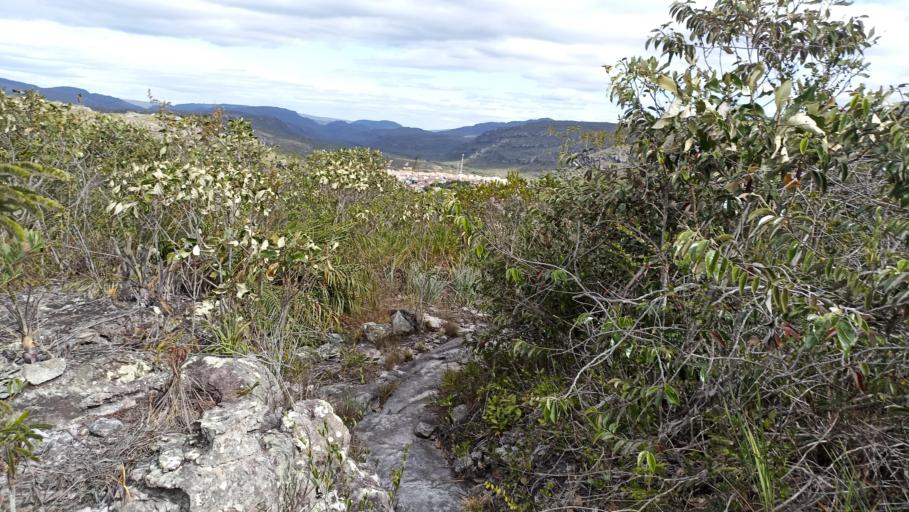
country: BR
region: Bahia
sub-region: Andarai
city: Vera Cruz
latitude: -12.9966
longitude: -41.3765
